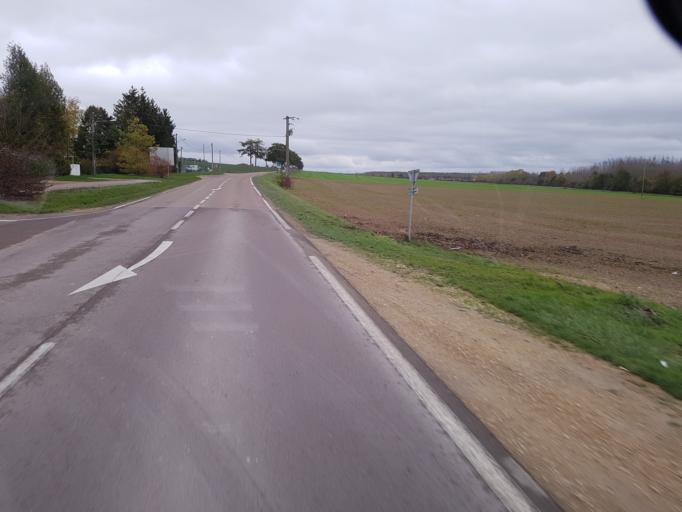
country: FR
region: Champagne-Ardenne
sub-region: Departement de l'Aube
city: Mery-sur-Seine
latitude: 48.4765
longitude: 3.8727
